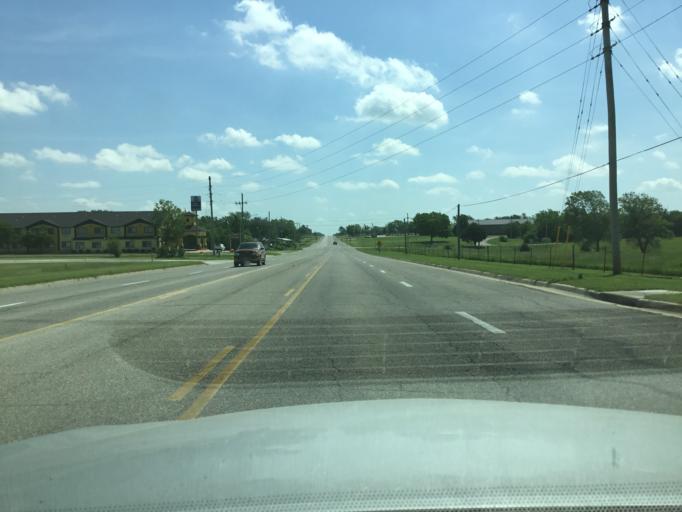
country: US
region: Kansas
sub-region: Labette County
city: Parsons
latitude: 37.3402
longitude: -95.2336
